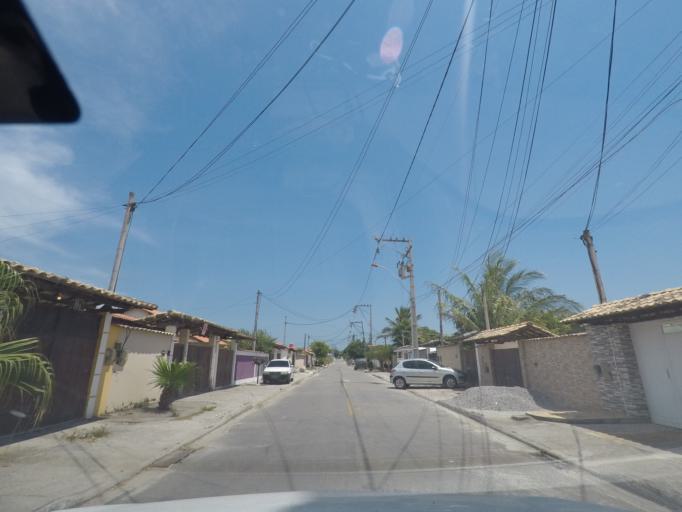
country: BR
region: Rio de Janeiro
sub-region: Niteroi
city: Niteroi
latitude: -22.9607
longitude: -42.9694
